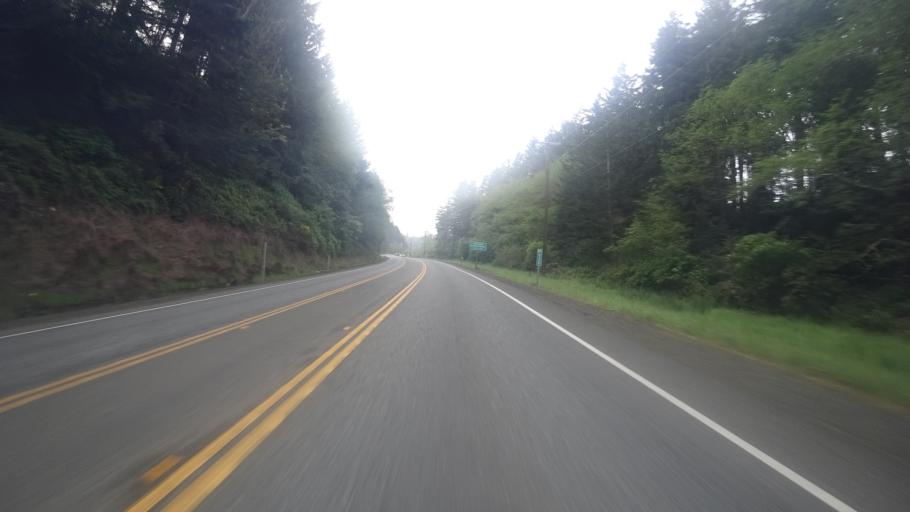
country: US
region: Oregon
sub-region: Coos County
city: North Bend
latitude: 43.4546
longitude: -124.2286
